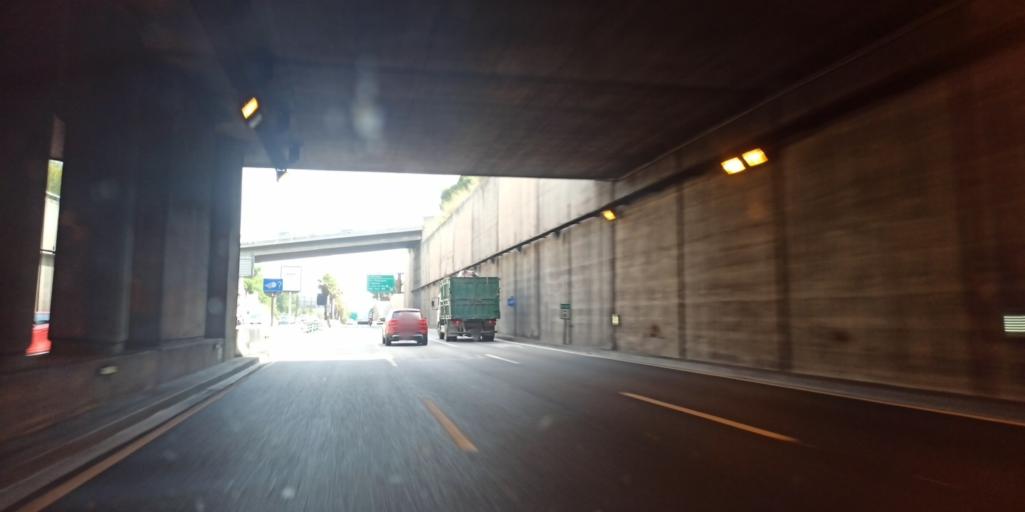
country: ES
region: Catalonia
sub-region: Provincia de Barcelona
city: les Corts
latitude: 41.3940
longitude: 2.1100
